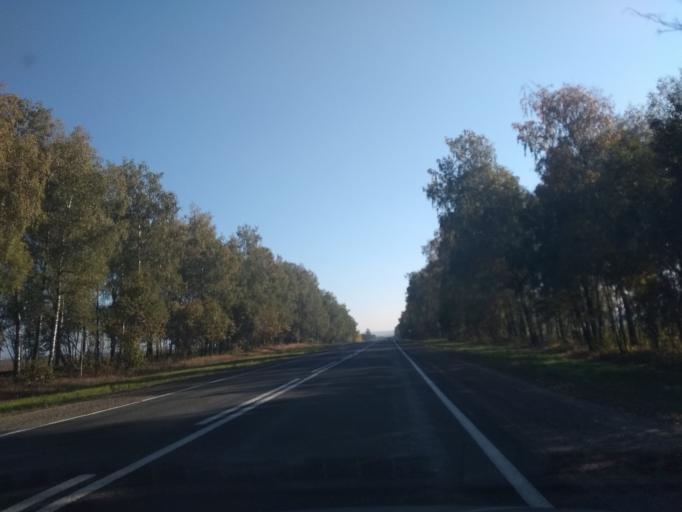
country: BY
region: Grodnenskaya
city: Slonim
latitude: 53.1219
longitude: 25.0944
